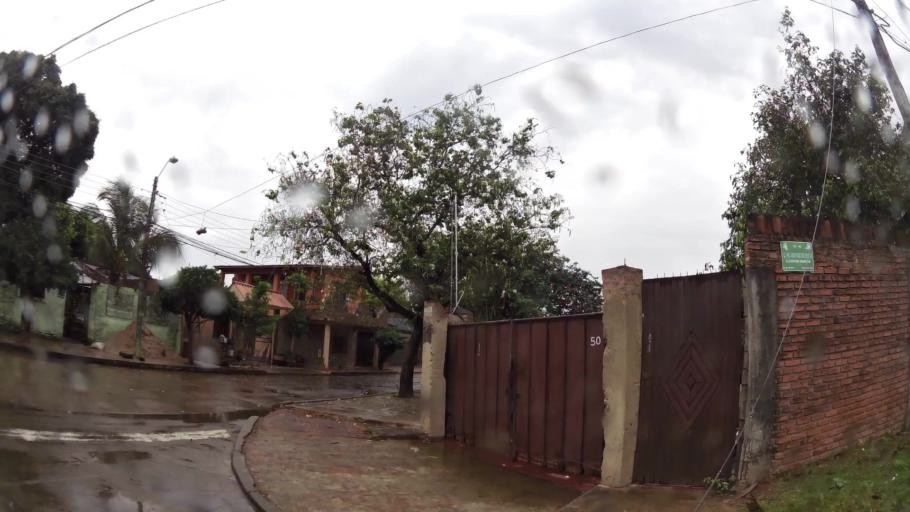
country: BO
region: Santa Cruz
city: Santa Cruz de la Sierra
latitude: -17.8018
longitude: -63.1562
